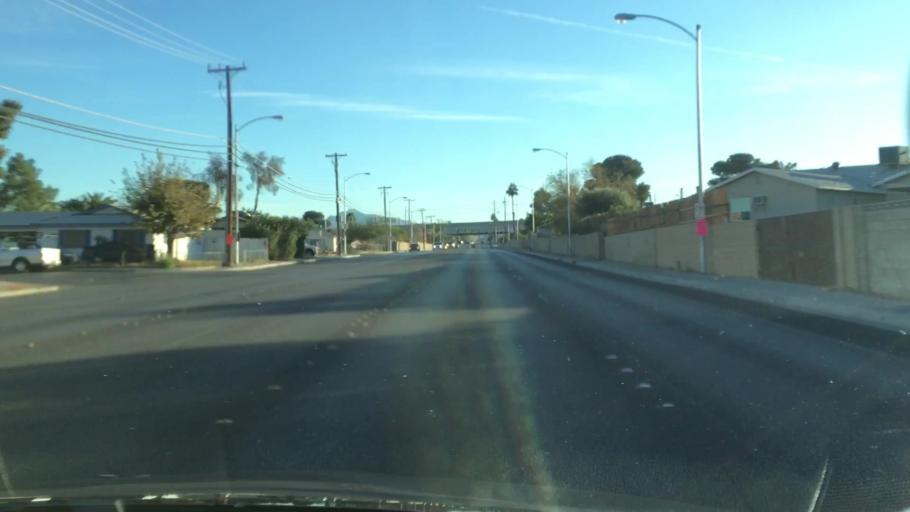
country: US
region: Nevada
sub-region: Clark County
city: Whitney
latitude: 36.0967
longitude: -115.0733
